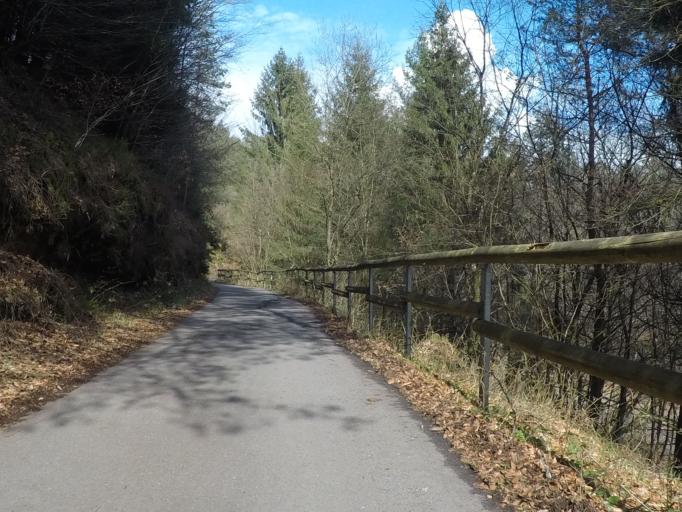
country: DE
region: Rheinland-Pfalz
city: Hinterweidenthal
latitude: 49.2106
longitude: 7.7305
